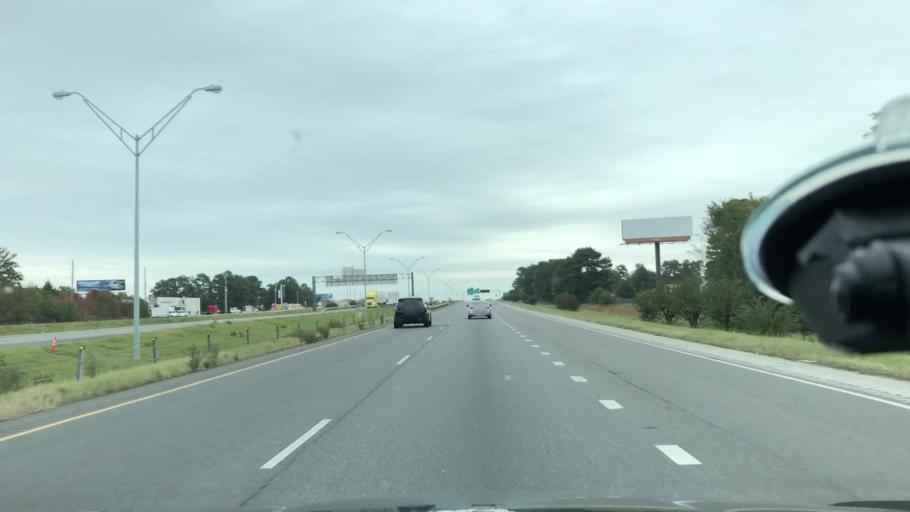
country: US
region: Arkansas
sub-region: Miller County
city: Texarkana
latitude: 33.4717
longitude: -94.0267
